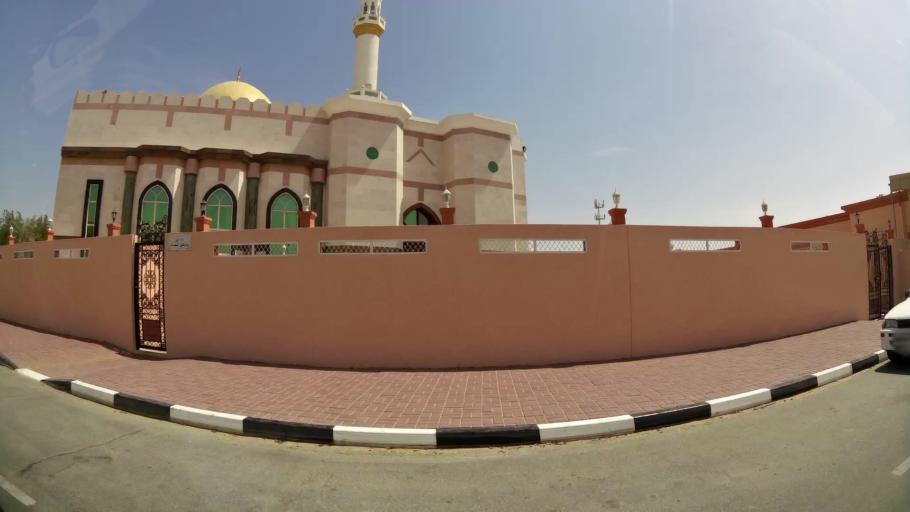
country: AE
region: Ash Shariqah
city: Sharjah
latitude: 25.1879
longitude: 55.4232
